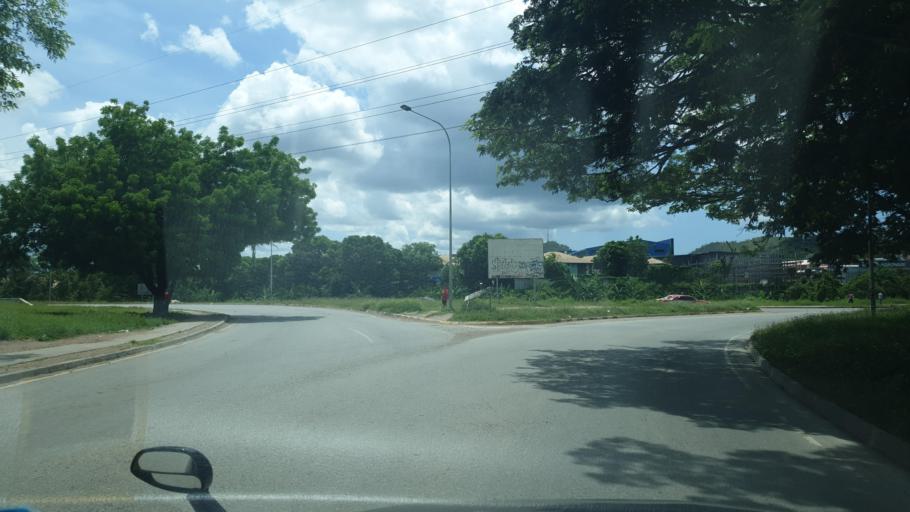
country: PG
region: National Capital
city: Port Moresby
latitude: -9.3969
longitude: 147.1600
